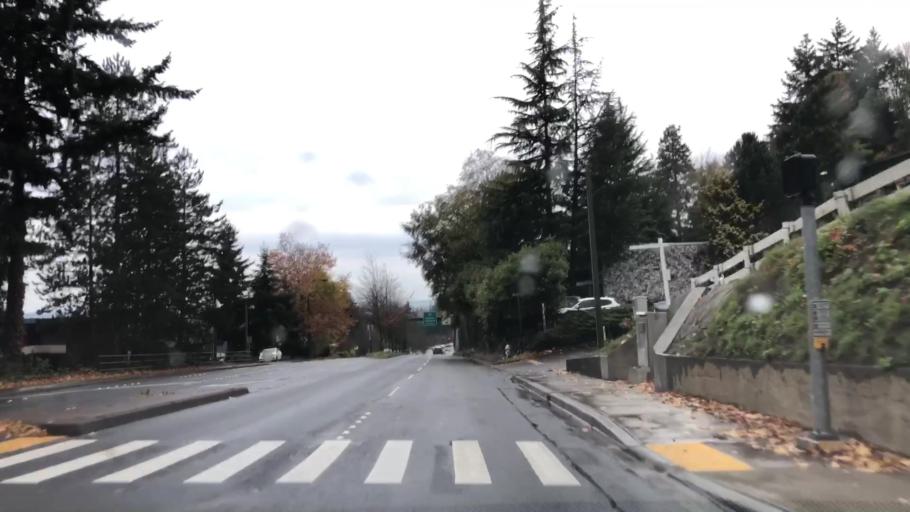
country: US
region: Washington
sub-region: King County
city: Mercer Island
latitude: 47.5816
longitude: -122.2306
